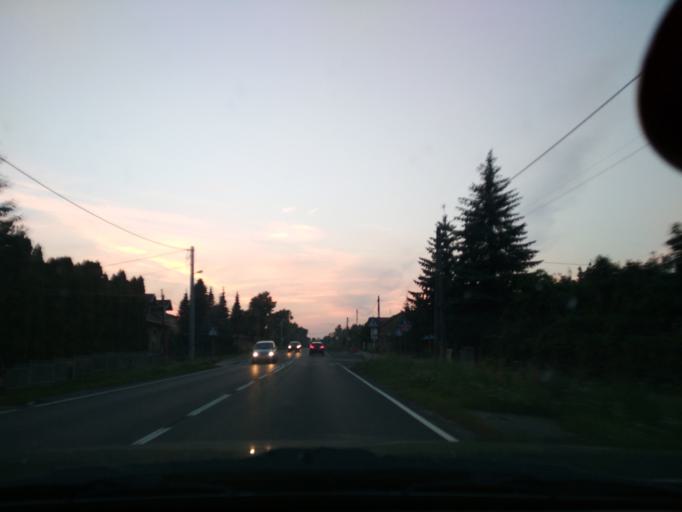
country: PL
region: Silesian Voivodeship
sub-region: Powiat zawiercianski
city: Ogrodzieniec
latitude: 50.4699
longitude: 19.4839
